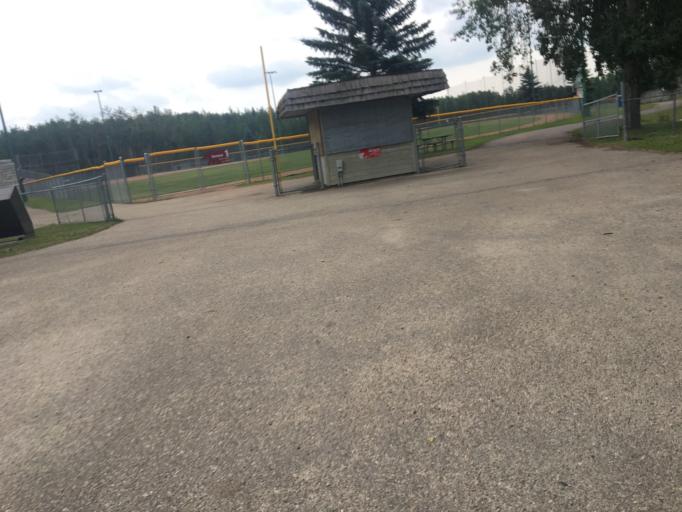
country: CA
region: Alberta
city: Grande Prairie
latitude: 55.1351
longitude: -118.7934
